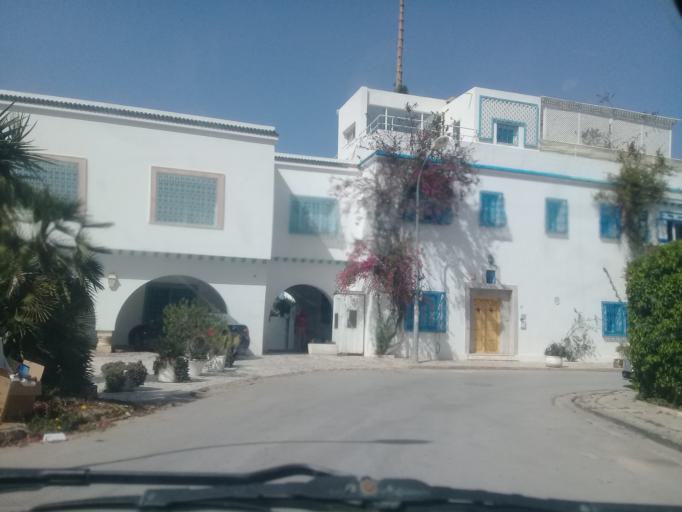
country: TN
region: Tunis
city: Al Marsa
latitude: 36.8883
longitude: 10.3270
